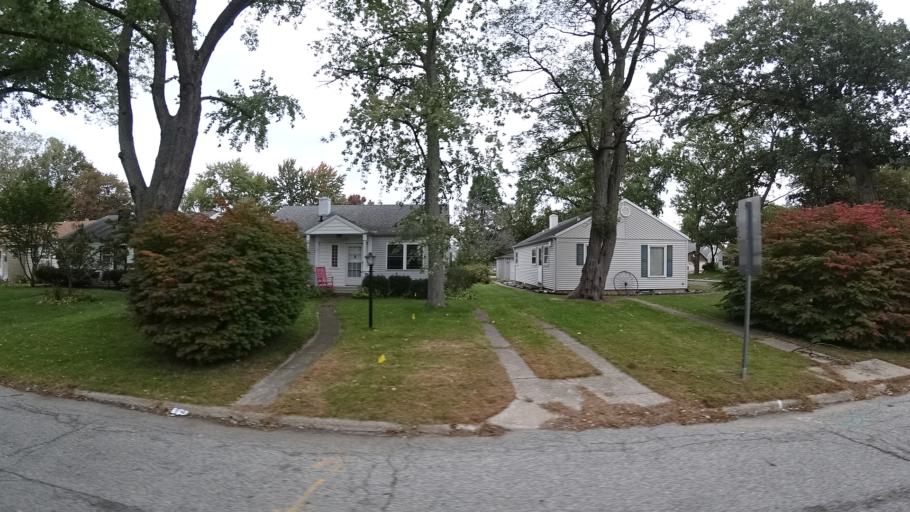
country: US
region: Indiana
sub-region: LaPorte County
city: Michigan City
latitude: 41.6976
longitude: -86.8868
